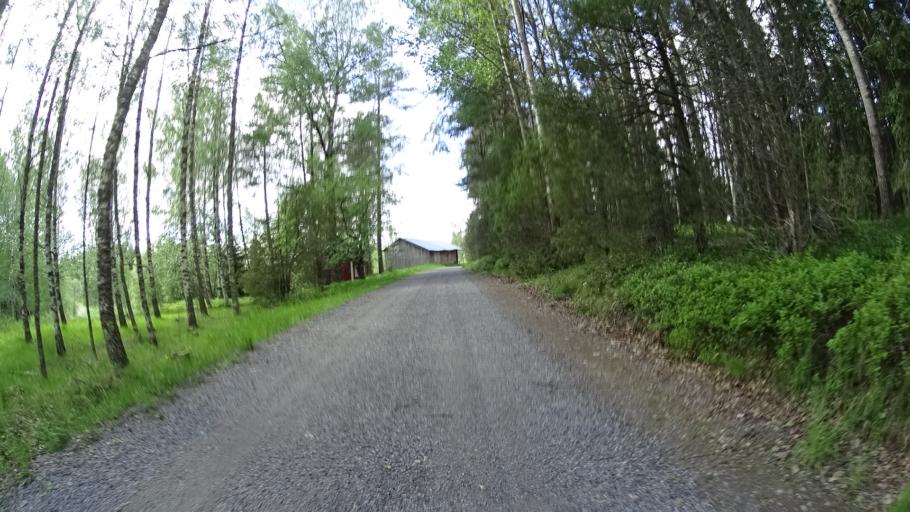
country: FI
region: Varsinais-Suomi
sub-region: Salo
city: Kisko
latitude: 60.1958
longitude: 23.5495
